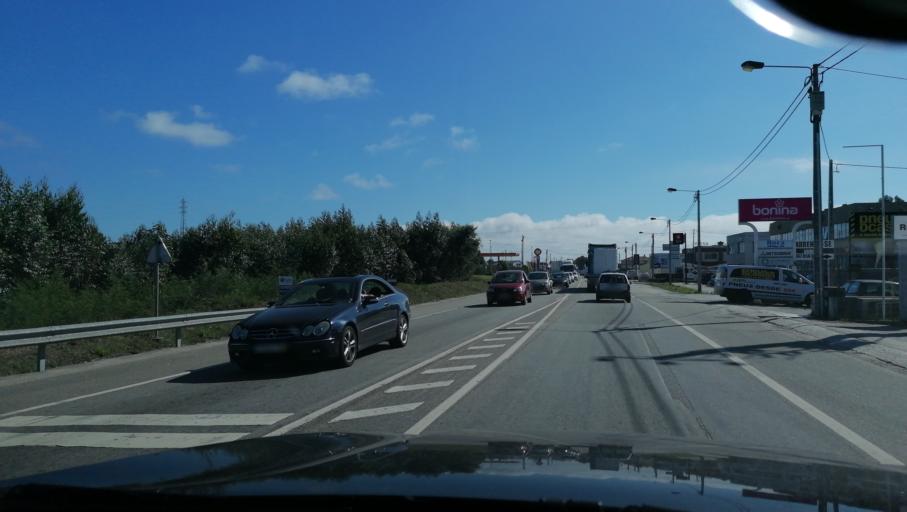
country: PT
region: Aveiro
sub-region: Aveiro
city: Aveiro
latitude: 40.6673
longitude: -8.6088
